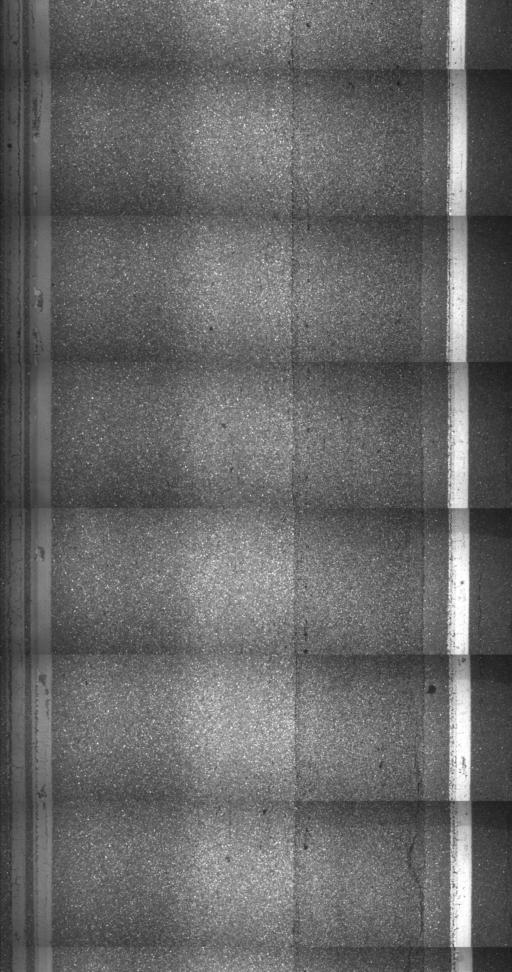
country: US
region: Vermont
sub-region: Bennington County
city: North Bennington
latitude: 42.9975
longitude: -73.2011
